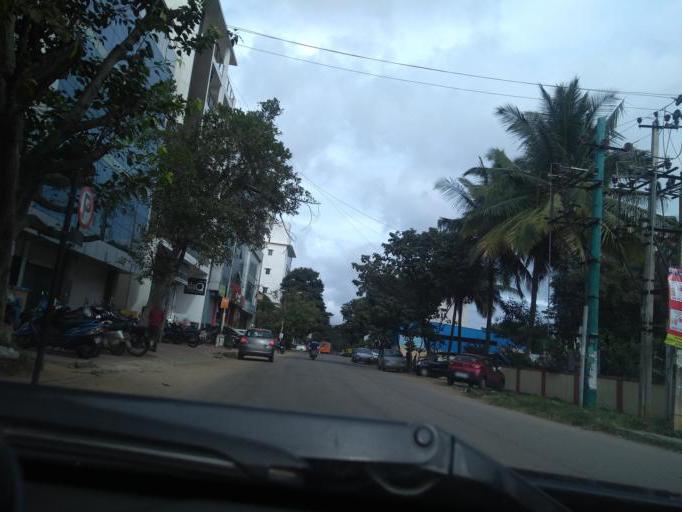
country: IN
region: Karnataka
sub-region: Bangalore Urban
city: Bangalore
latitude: 13.0111
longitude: 77.6591
